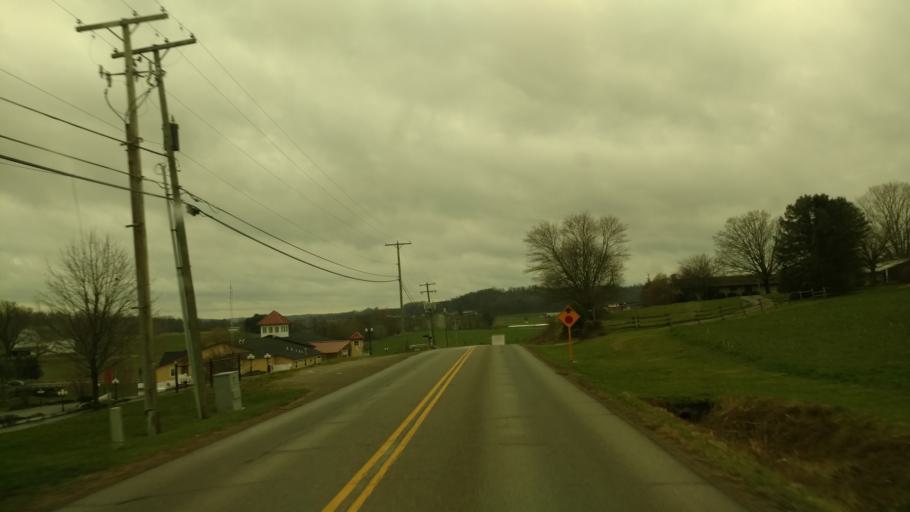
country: US
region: Ohio
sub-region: Holmes County
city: Millersburg
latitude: 40.5574
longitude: -81.8210
